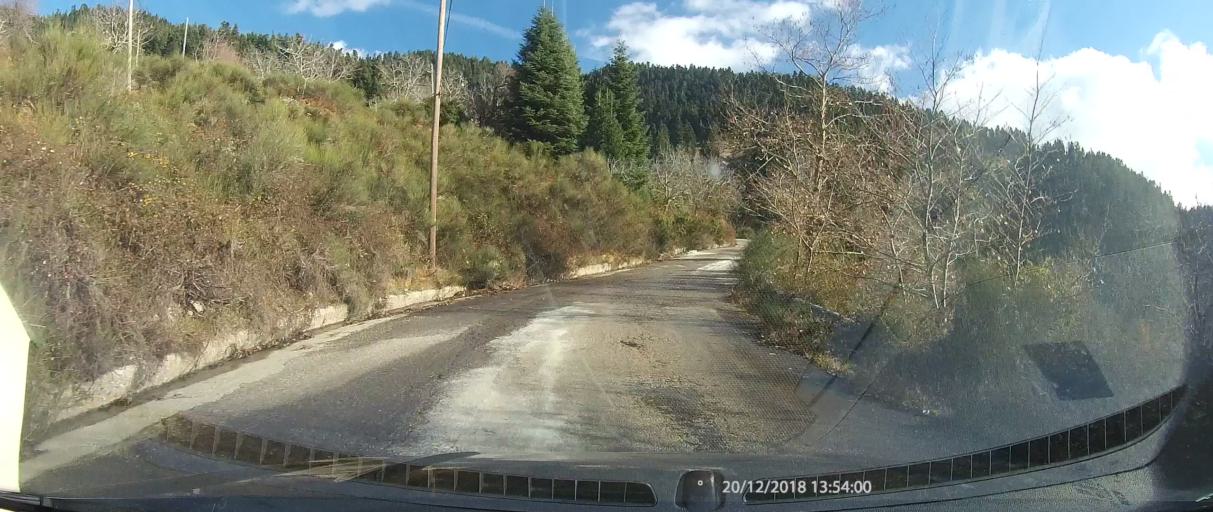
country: GR
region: West Greece
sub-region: Nomos Aitolias kai Akarnanias
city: Paravola
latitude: 38.7129
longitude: 21.6084
